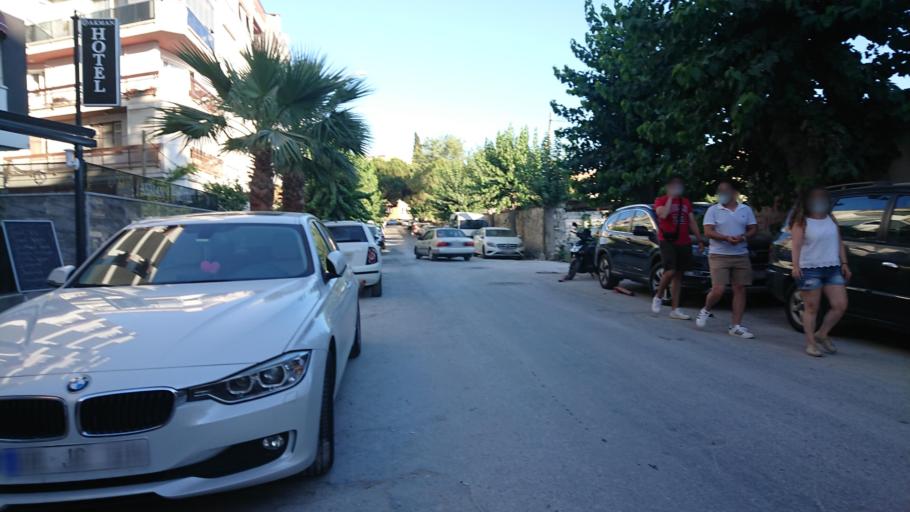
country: TR
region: Aydin
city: Kusadasi
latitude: 37.8645
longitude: 27.2636
